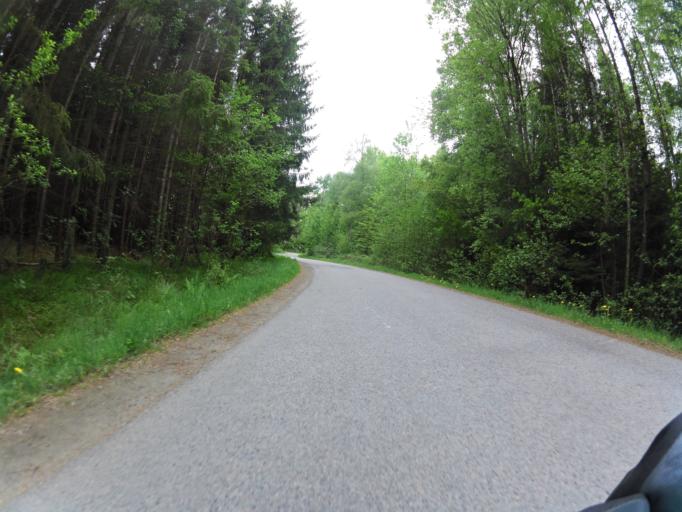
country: NO
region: Ostfold
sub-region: Moss
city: Moss
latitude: 59.3922
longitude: 10.6530
